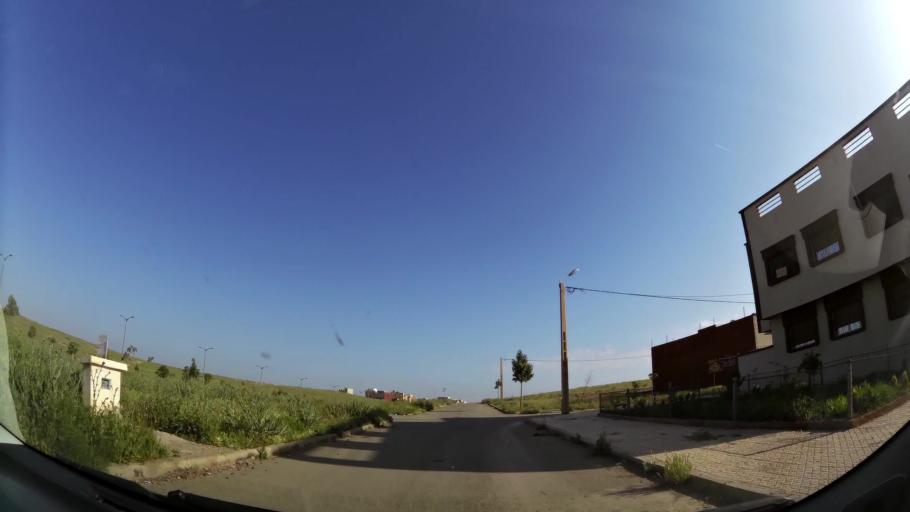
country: MA
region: Oriental
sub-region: Oujda-Angad
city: Oujda
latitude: 34.6758
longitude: -1.9467
